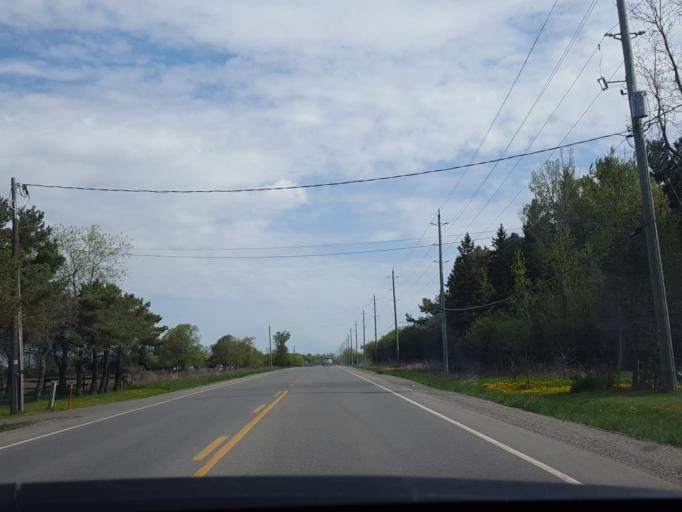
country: CA
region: Ontario
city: Uxbridge
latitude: 44.1632
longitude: -78.8968
